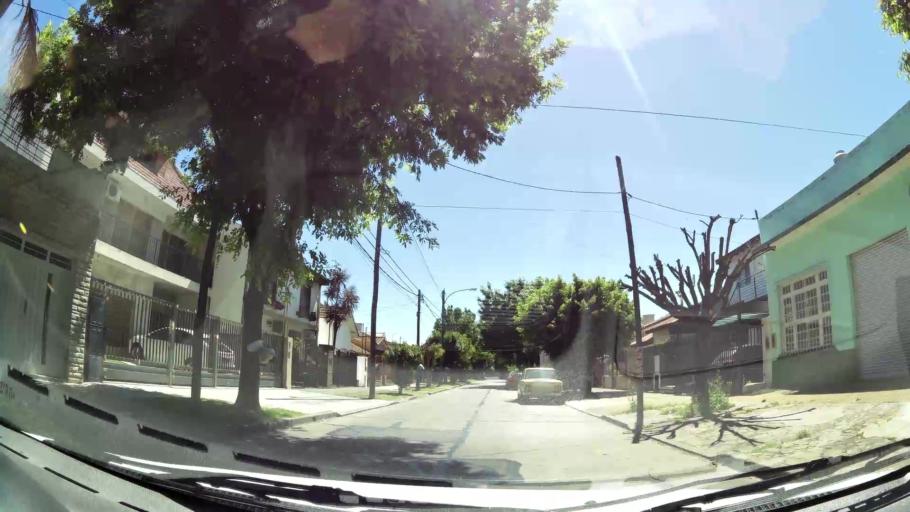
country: AR
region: Buenos Aires
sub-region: Partido de General San Martin
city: General San Martin
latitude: -34.5303
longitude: -58.5420
